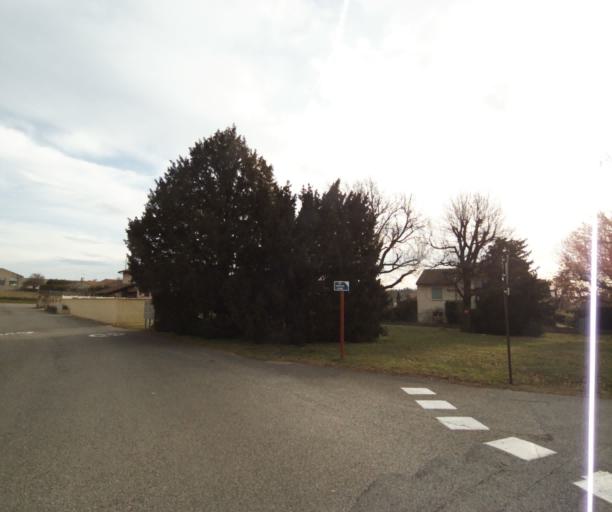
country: FR
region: Rhone-Alpes
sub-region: Departement de l'Ardeche
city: Davezieux
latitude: 45.2528
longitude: 4.6976
